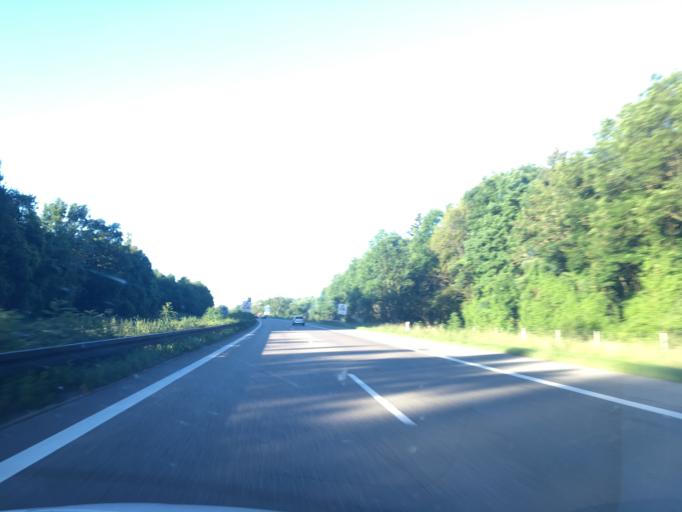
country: DE
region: Bavaria
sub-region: Swabia
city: Altenstadt
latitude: 48.1390
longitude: 10.1120
